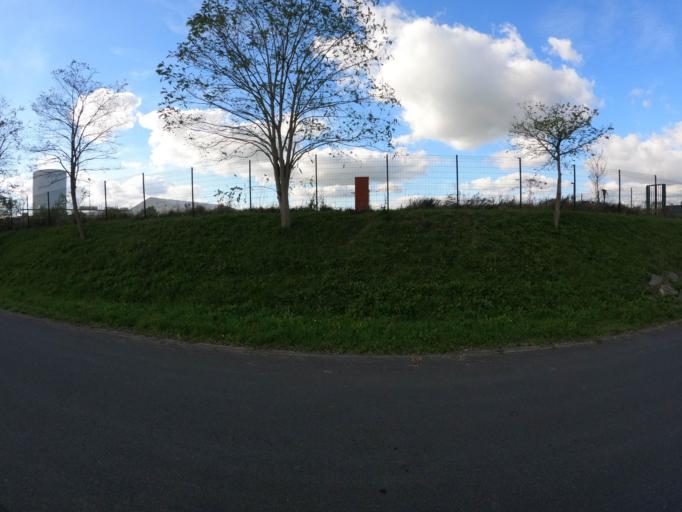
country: FR
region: Pays de la Loire
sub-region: Departement de la Loire-Atlantique
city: Le Bignon
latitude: 47.0997
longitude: -1.4489
